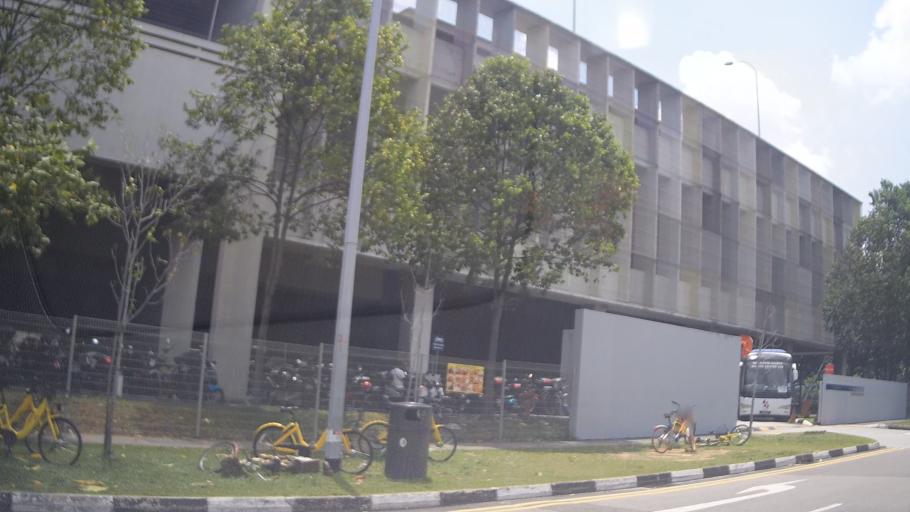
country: MY
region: Johor
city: Johor Bahru
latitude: 1.4524
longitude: 103.7945
